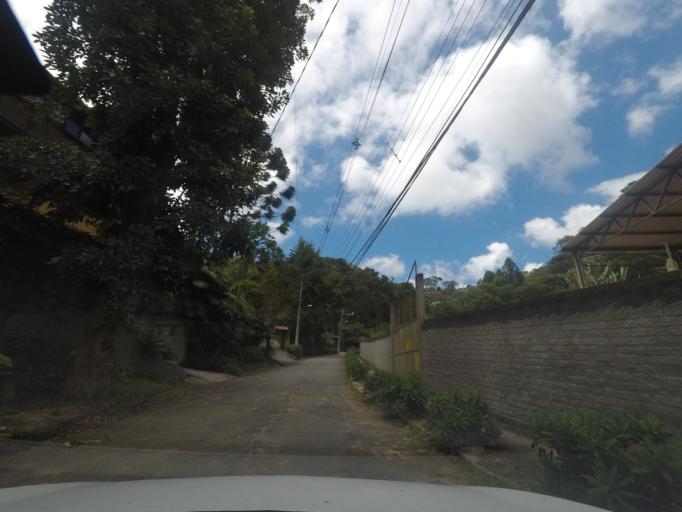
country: BR
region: Rio de Janeiro
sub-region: Teresopolis
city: Teresopolis
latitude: -22.4038
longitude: -42.9806
